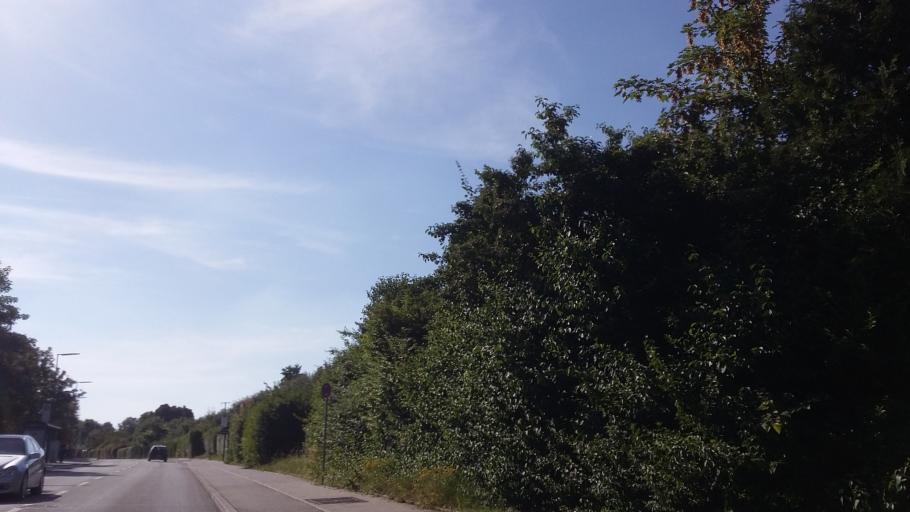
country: DE
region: Bavaria
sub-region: Upper Bavaria
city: Pasing
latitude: 48.1506
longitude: 11.4554
